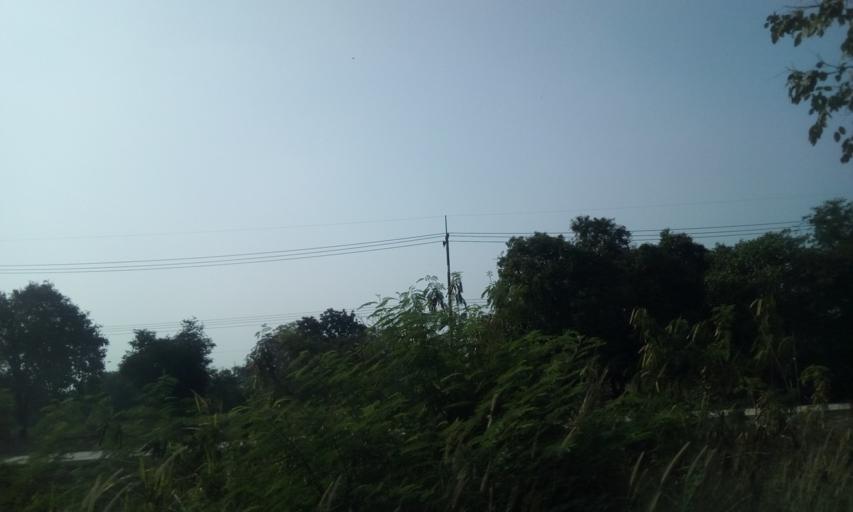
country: TH
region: Sing Buri
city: Tha Chang
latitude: 14.7398
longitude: 100.4372
